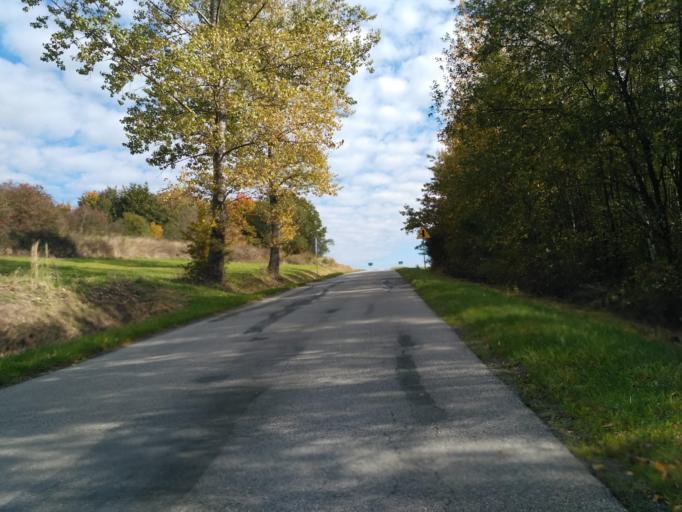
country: PL
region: Subcarpathian Voivodeship
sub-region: Powiat debicki
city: Brzostek
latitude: 49.8913
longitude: 21.3453
